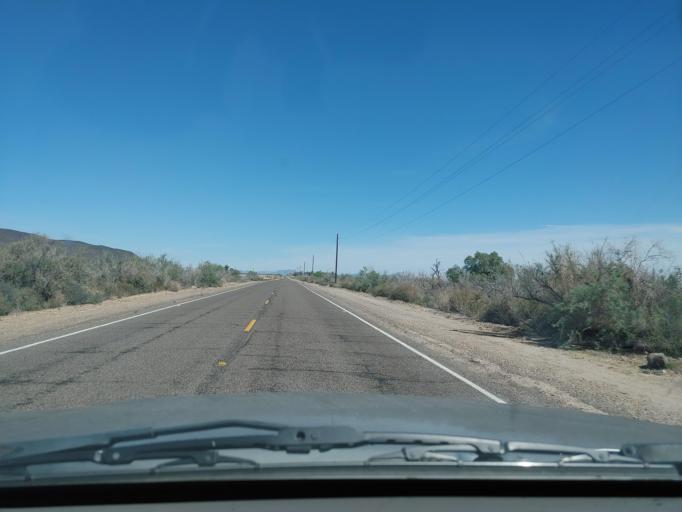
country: US
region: Arizona
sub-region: Maricopa County
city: Gila Bend
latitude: 32.9734
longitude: -113.3060
